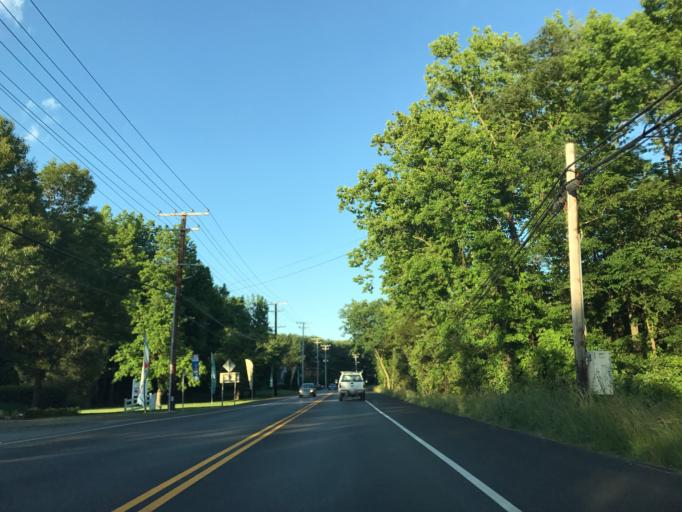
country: US
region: Maryland
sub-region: Anne Arundel County
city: Davidsonville
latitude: 38.9281
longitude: -76.6165
